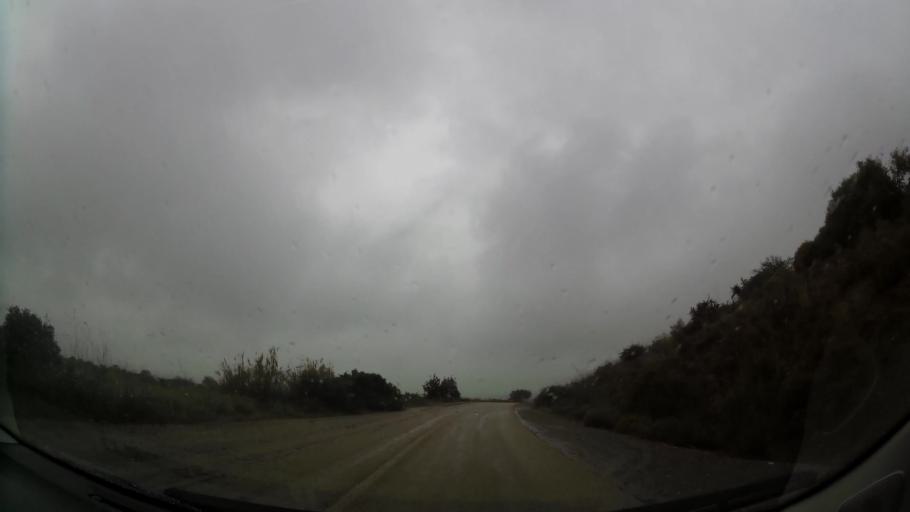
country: MA
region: Taza-Al Hoceima-Taounate
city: Imzourene
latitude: 35.1190
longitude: -3.7796
